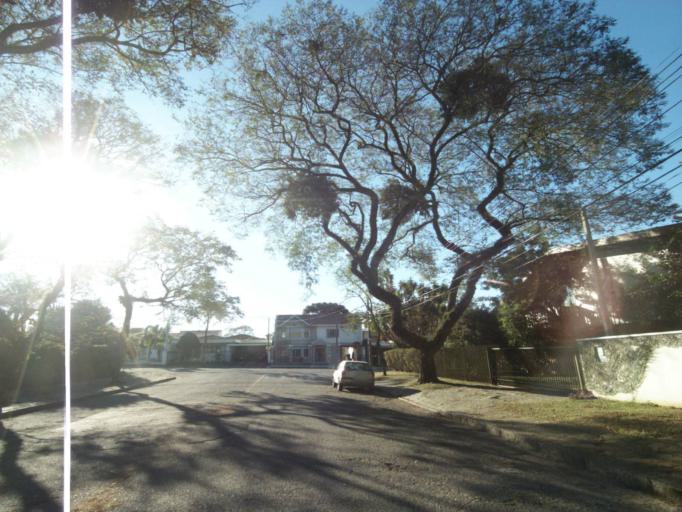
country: BR
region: Parana
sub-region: Curitiba
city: Curitiba
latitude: -25.4216
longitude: -49.2309
